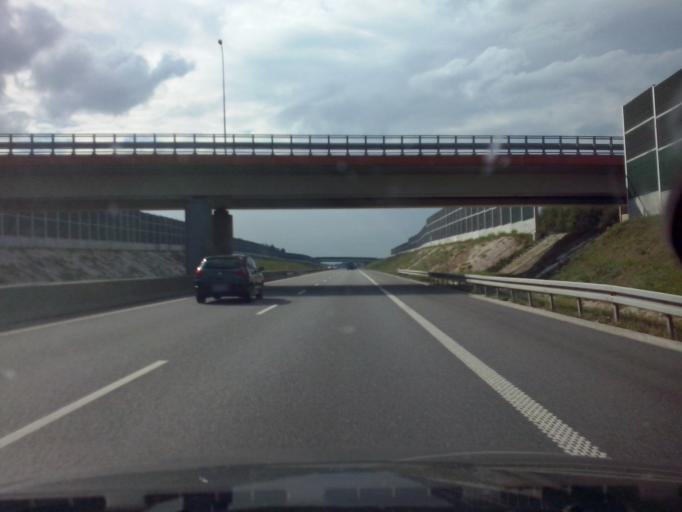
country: PL
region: Lesser Poland Voivodeship
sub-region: Powiat brzeski
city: Maszkienice
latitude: 50.0039
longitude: 20.6907
